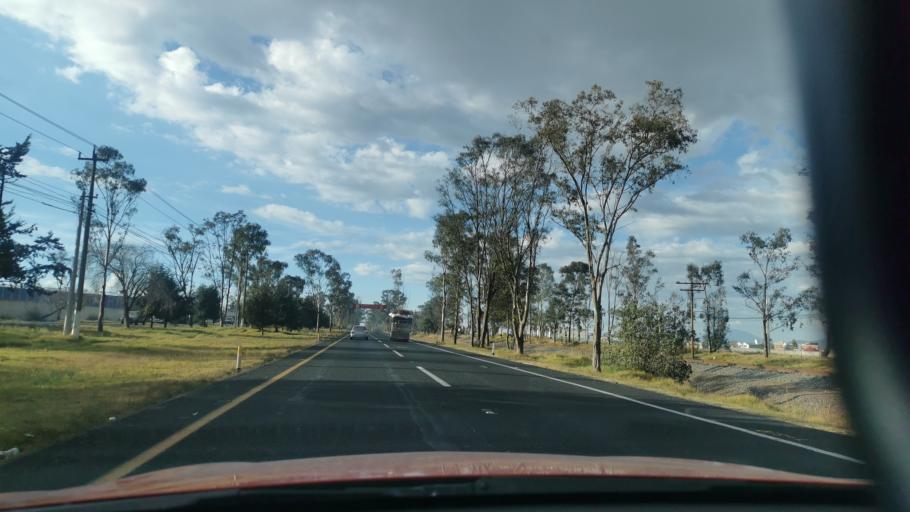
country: MX
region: Mexico
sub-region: Toluca
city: Colonia Aviacion Autopan
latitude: 19.3713
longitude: -99.6964
